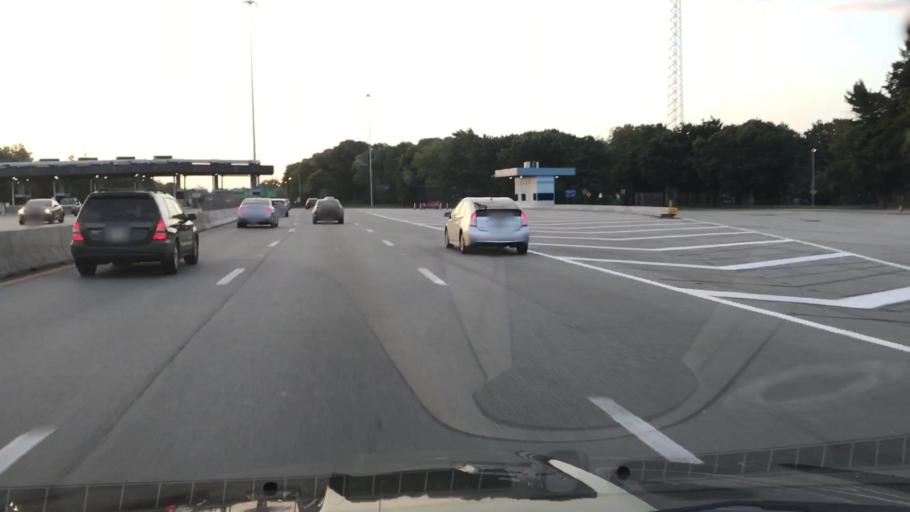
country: US
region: New Jersey
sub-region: Camden County
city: Pennsauken
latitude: 39.9797
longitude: -75.0544
